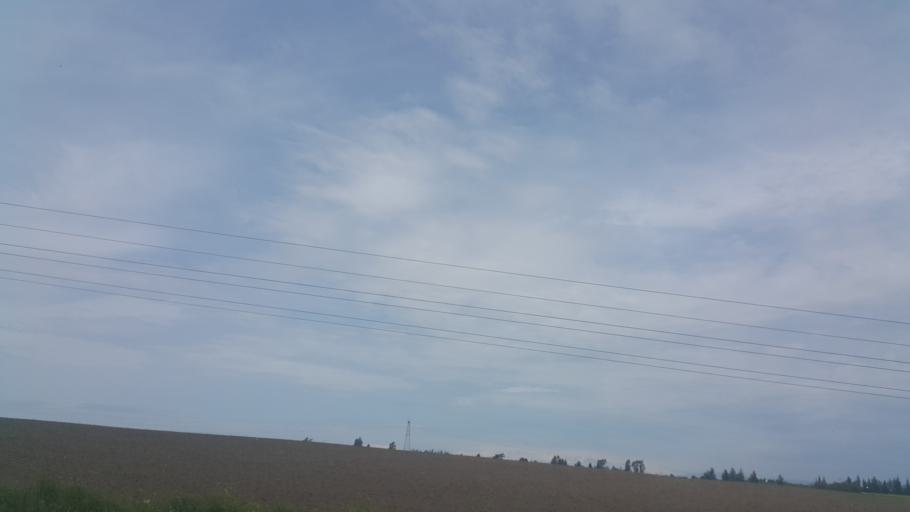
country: TR
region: Adana
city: Yakapinar
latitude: 36.9989
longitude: 35.6841
